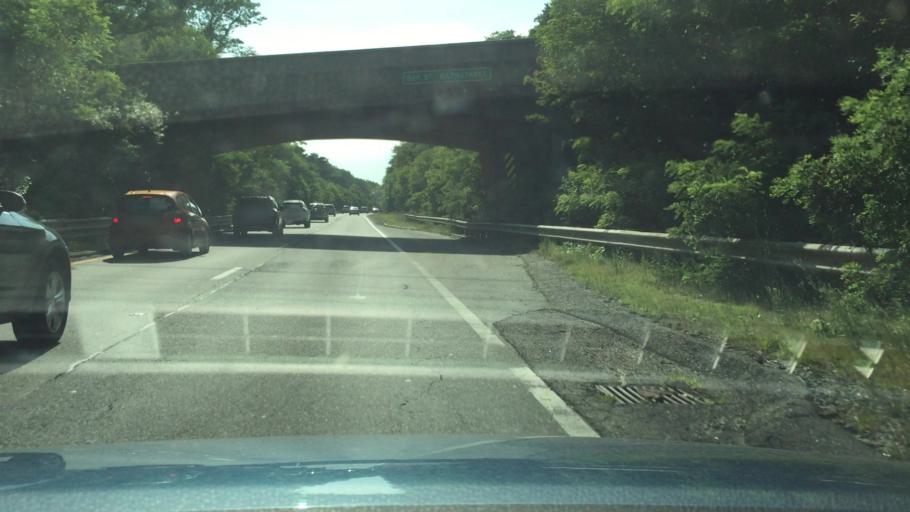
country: US
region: Massachusetts
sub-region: Barnstable County
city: West Barnstable
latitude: 41.6846
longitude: -70.3532
